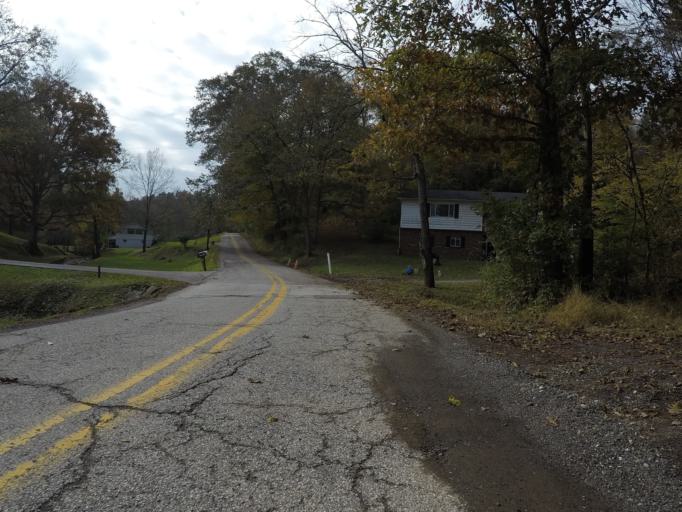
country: US
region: West Virginia
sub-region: Cabell County
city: Huntington
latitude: 38.3773
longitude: -82.4046
